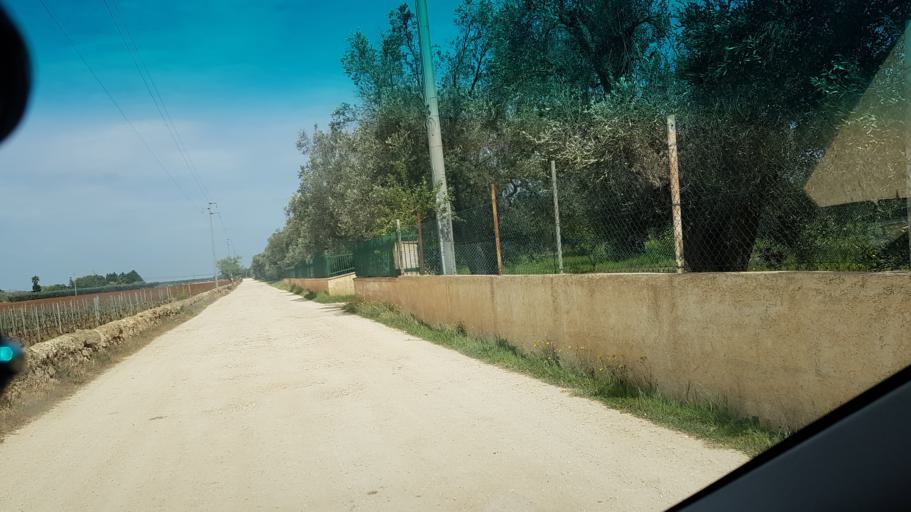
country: IT
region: Apulia
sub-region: Provincia di Brindisi
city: Mesagne
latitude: 40.5987
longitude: 17.8552
